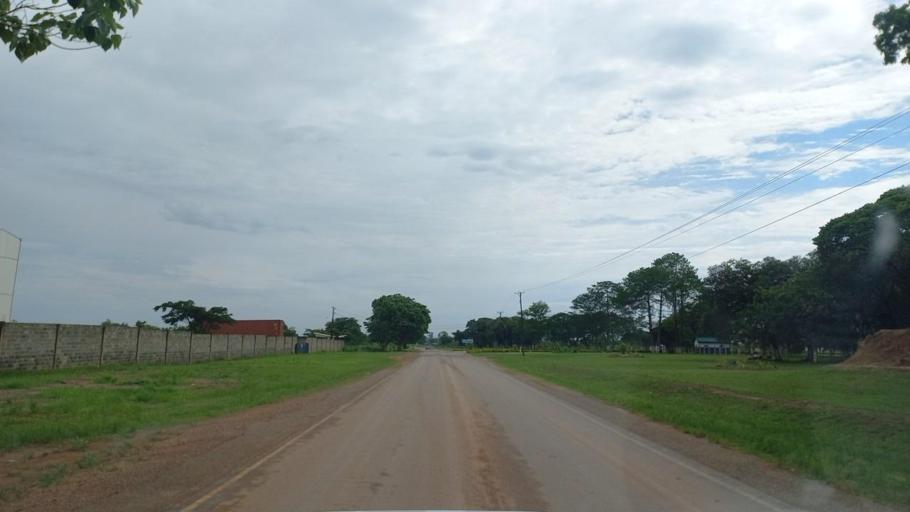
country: ZM
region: Copperbelt
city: Kitwe
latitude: -12.8838
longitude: 28.3165
